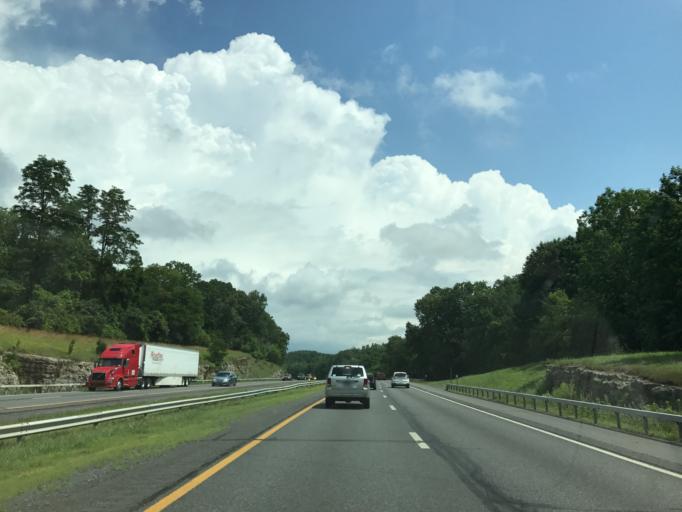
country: US
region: New York
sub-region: Greene County
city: Coxsackie
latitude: 42.3660
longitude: -73.8461
